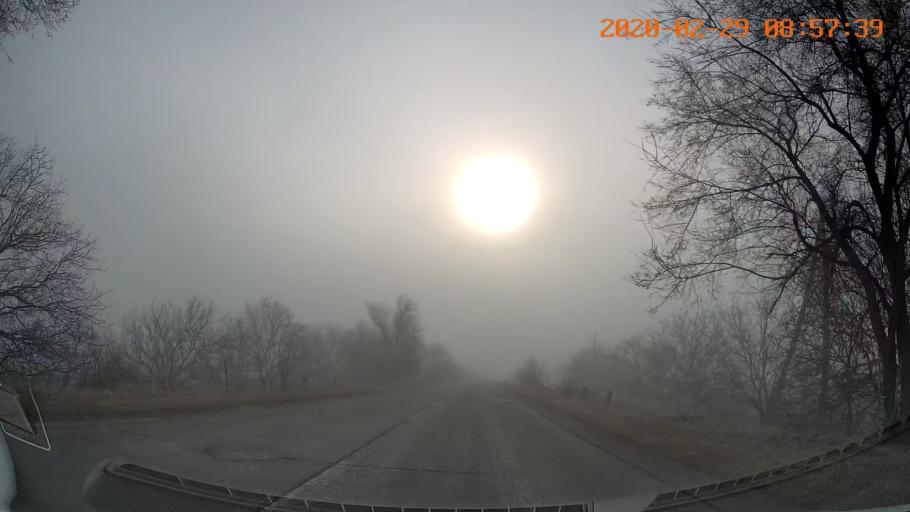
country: MD
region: Telenesti
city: Tiraspolul Nou
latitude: 46.9268
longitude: 29.6294
